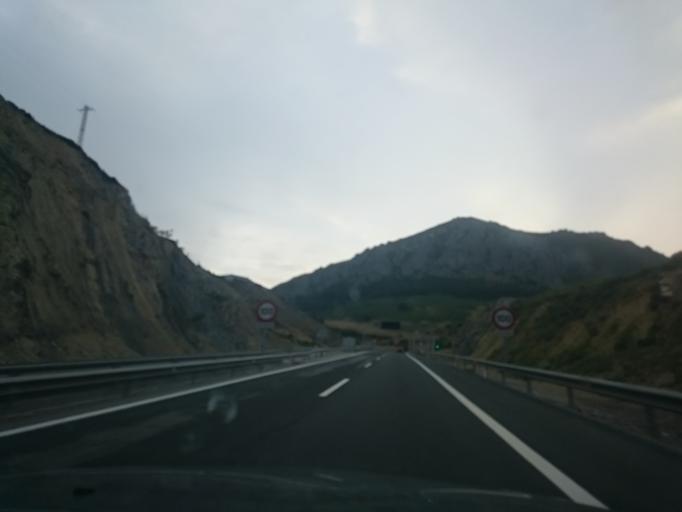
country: ES
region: Castille and Leon
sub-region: Provincia de Leon
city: Sena de Luna
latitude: 42.9379
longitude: -5.8454
